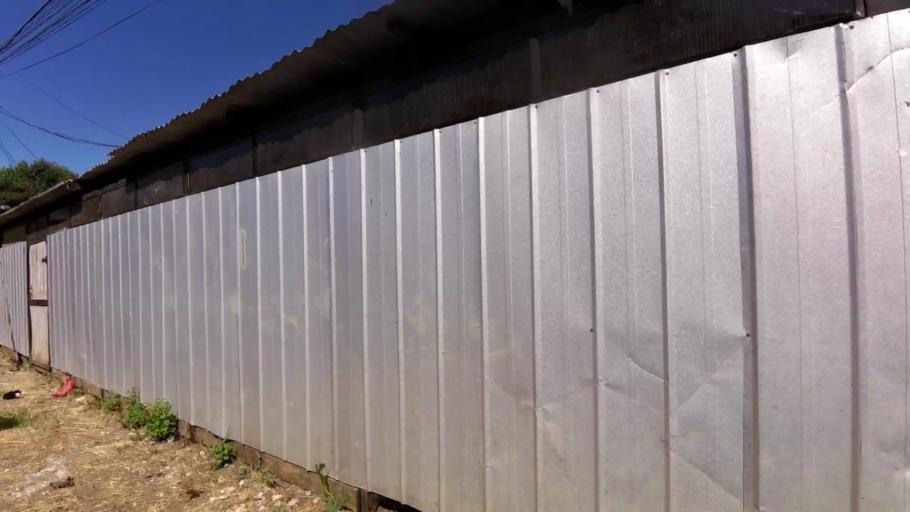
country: CL
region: Biobio
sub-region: Provincia de Concepcion
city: Concepcion
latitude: -36.7904
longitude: -73.0409
